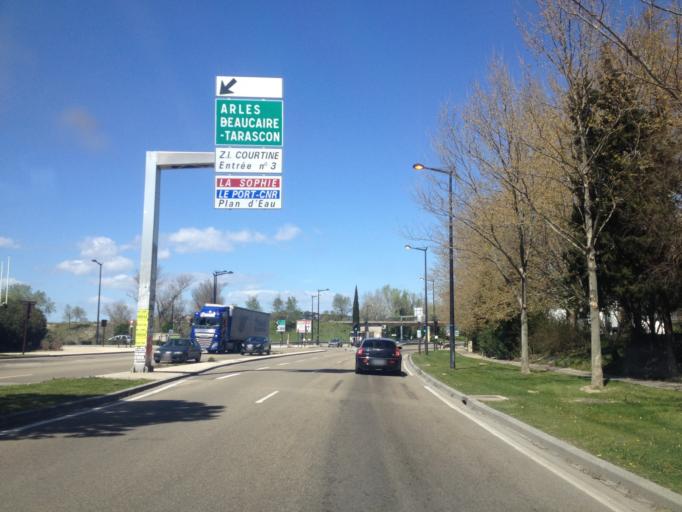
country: FR
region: Languedoc-Roussillon
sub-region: Departement du Gard
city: Les Angles
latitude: 43.9350
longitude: 4.7820
